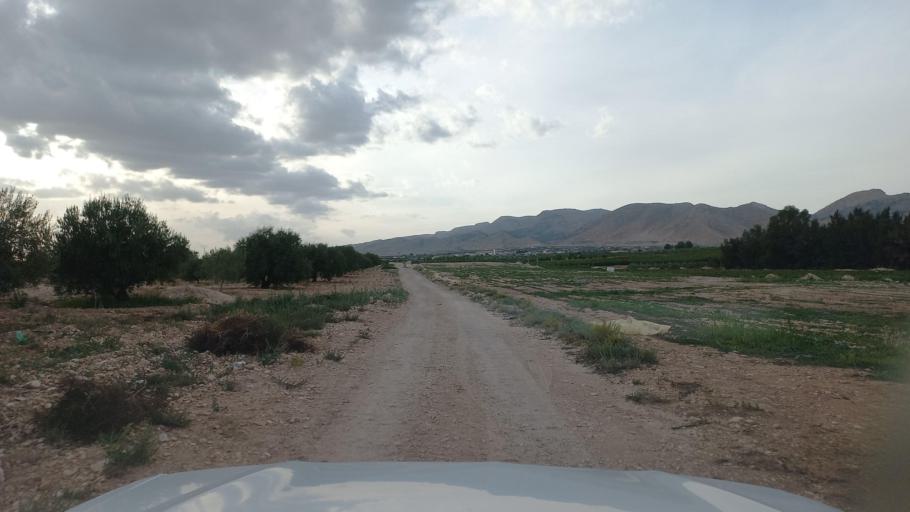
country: TN
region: Al Qasrayn
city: Sbiba
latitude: 35.4404
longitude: 9.0950
